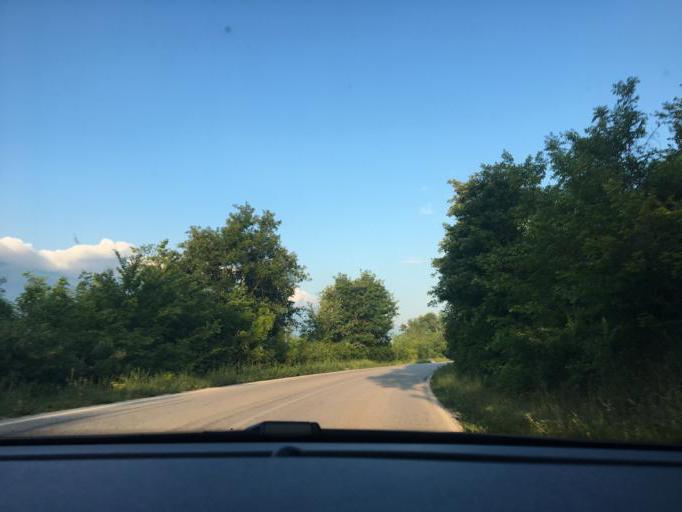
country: MK
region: Novo Selo
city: Novo Selo
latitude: 41.3955
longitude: 23.0238
